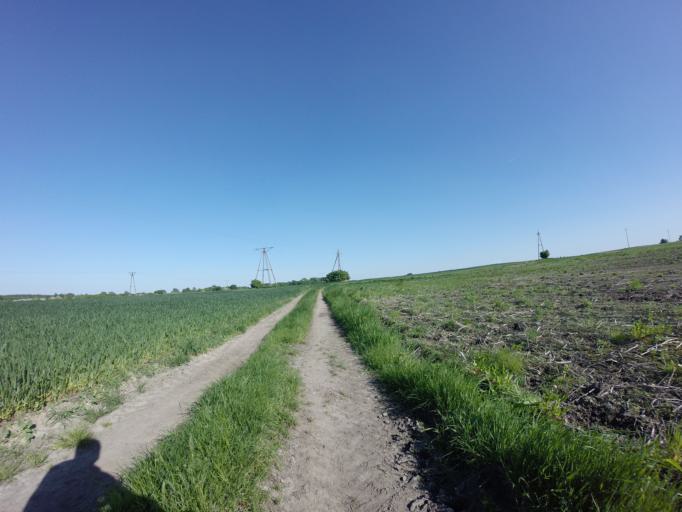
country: PL
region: West Pomeranian Voivodeship
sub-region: Powiat choszczenski
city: Choszczno
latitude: 53.1506
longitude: 15.4109
